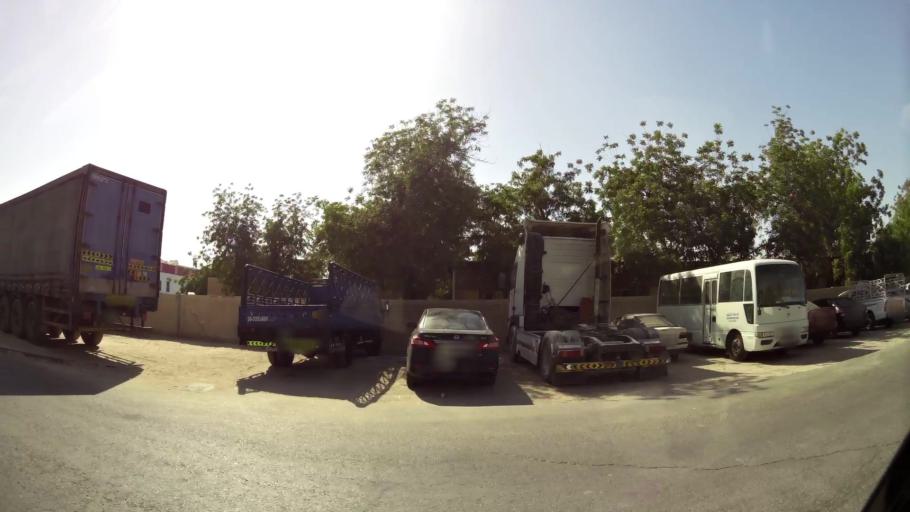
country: AE
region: Dubai
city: Dubai
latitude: 25.1261
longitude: 55.2276
